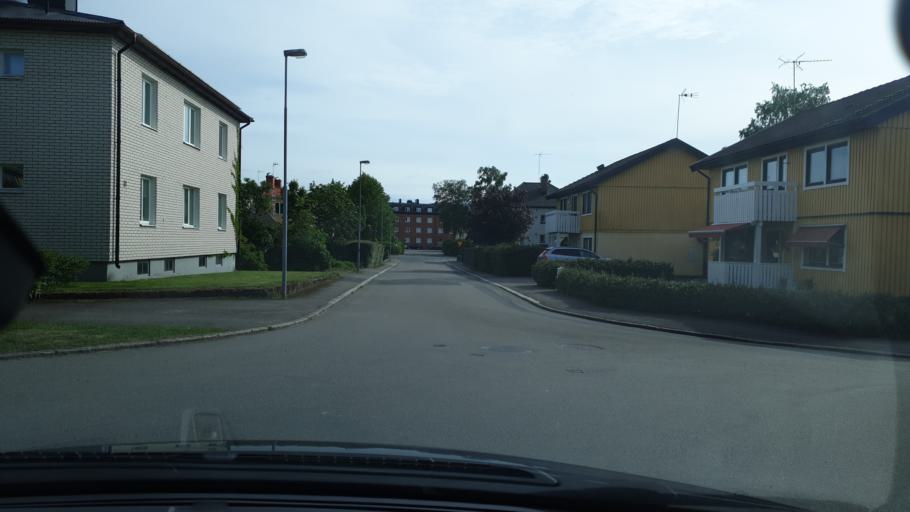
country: SE
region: Joenkoeping
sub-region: Vetlanda Kommun
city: Vetlanda
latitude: 57.4284
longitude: 15.0904
